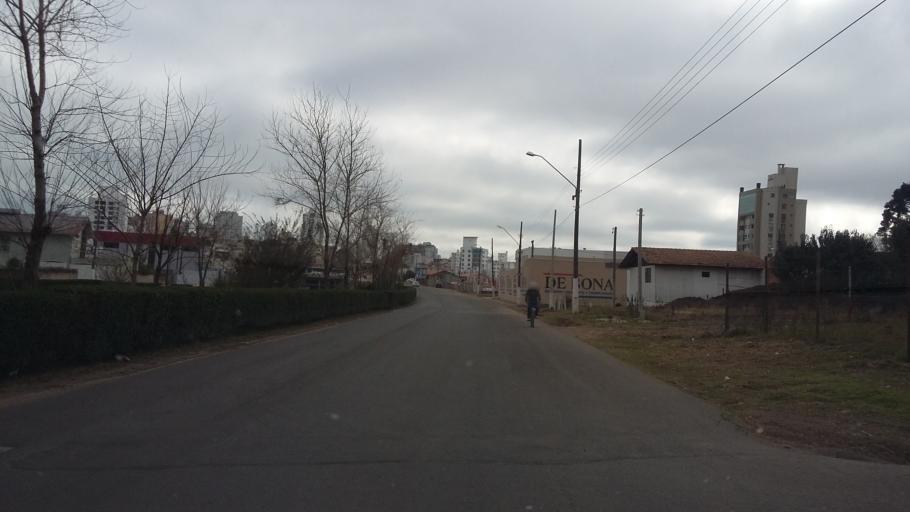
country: BR
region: Santa Catarina
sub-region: Lages
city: Lages
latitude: -27.8260
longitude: -50.3212
